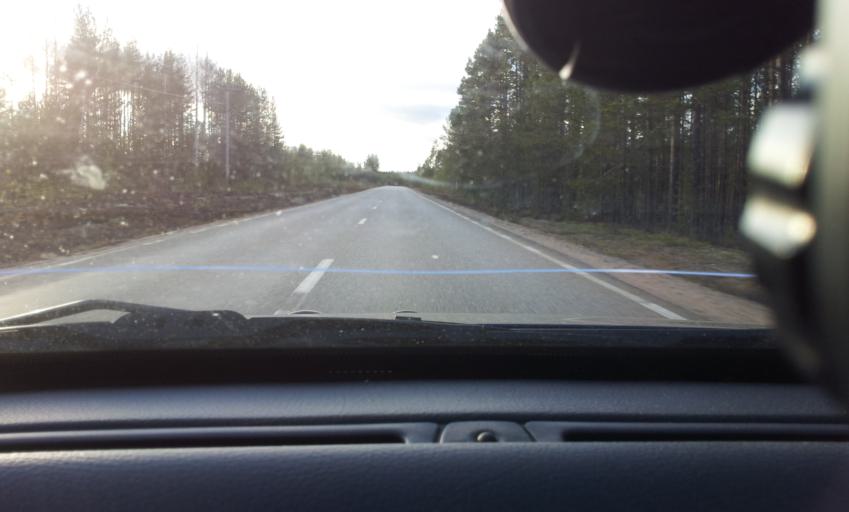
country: SE
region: Jaemtland
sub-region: Harjedalens Kommun
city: Sveg
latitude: 62.1136
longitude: 15.0533
